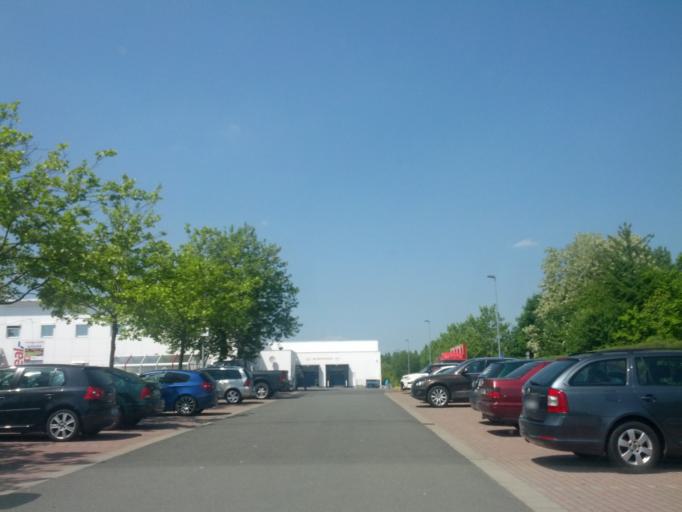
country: DE
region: Thuringia
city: Gotha
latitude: 50.9409
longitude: 10.6778
